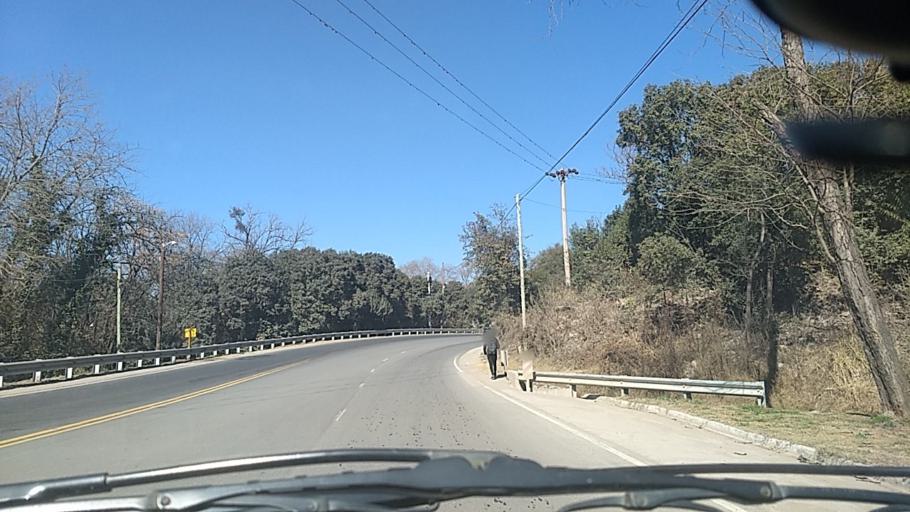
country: AR
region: Cordoba
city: Salsipuedes
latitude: -31.1090
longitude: -64.2913
